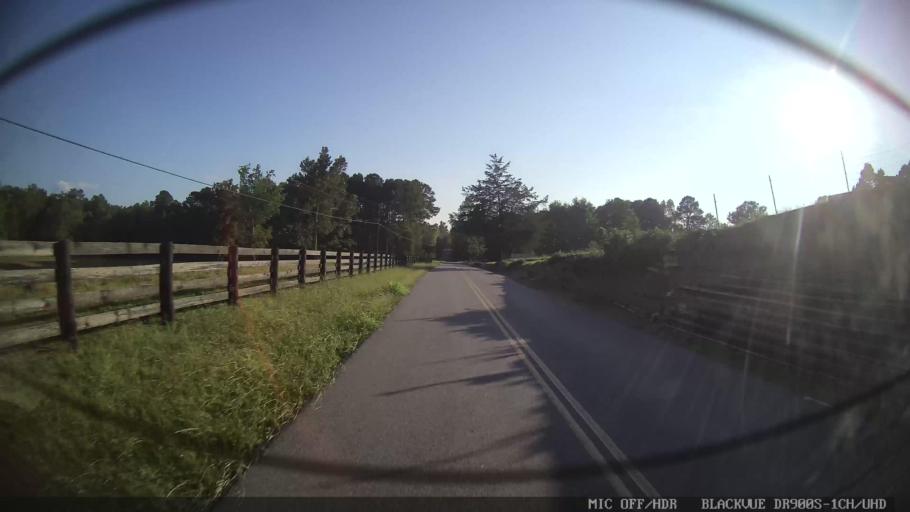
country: US
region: Tennessee
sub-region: Bradley County
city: Wildwood Lake
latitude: 35.0162
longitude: -84.7818
